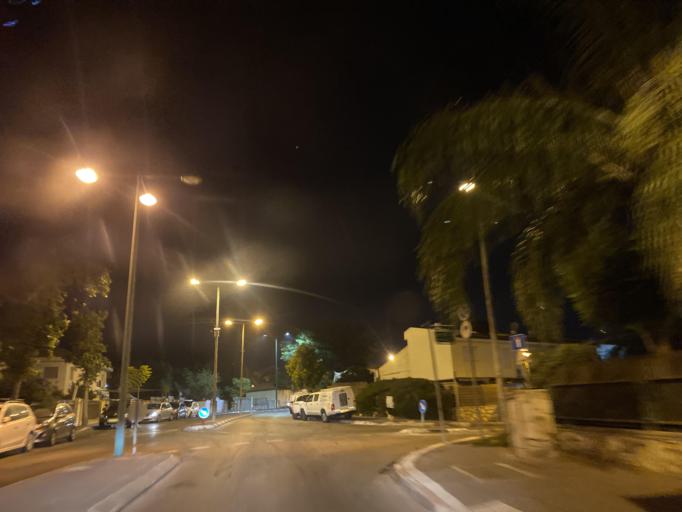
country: IL
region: Haifa
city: Daliyat el Karmil
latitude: 32.6411
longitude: 35.0839
